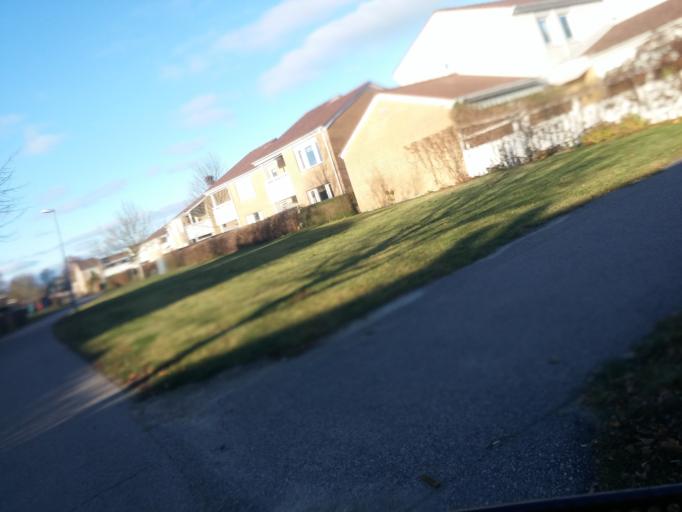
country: SE
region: Skane
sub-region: Angelholms Kommun
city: AEngelholm
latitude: 56.2274
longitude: 12.8336
